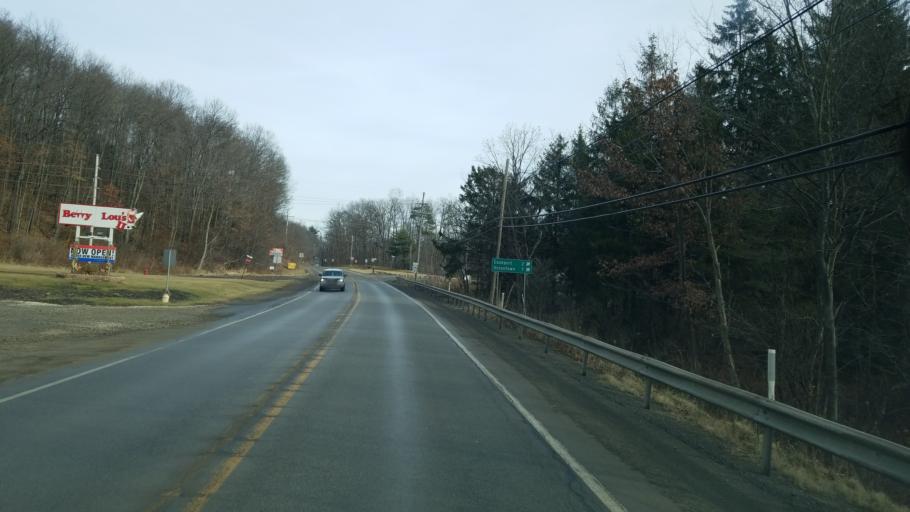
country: US
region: Pennsylvania
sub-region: Indiana County
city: Clymer
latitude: 40.7091
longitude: -78.9519
